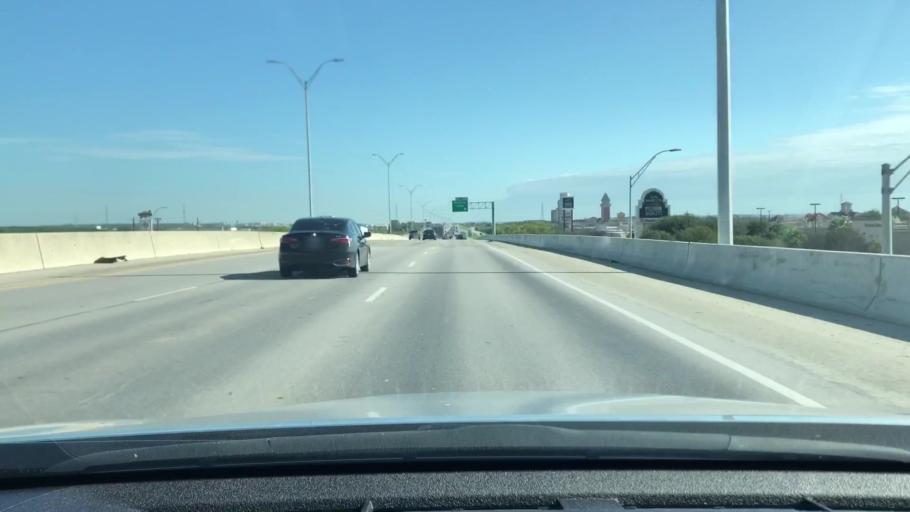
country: US
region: Texas
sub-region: Hays County
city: San Marcos
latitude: 29.8277
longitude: -97.9855
